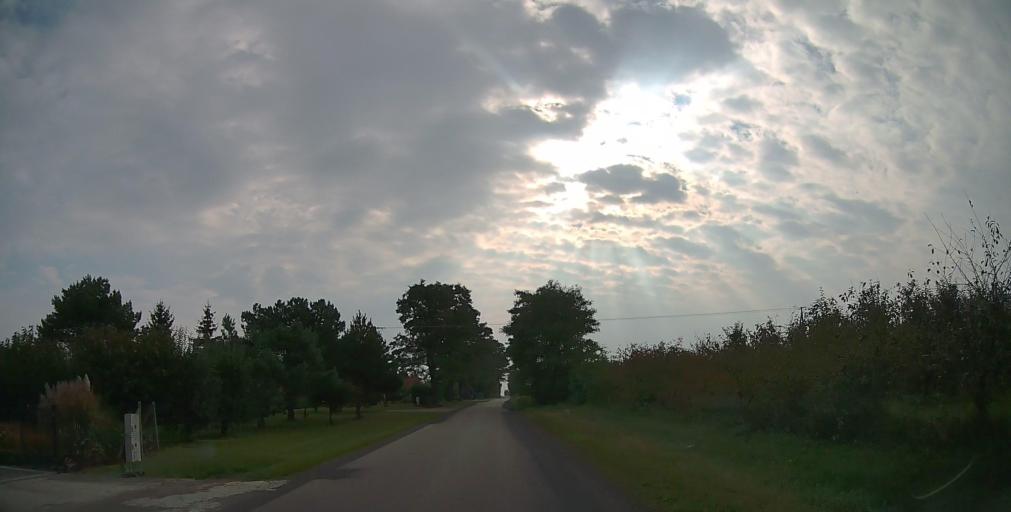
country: PL
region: Masovian Voivodeship
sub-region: Powiat grojecki
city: Mogielnica
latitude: 51.6571
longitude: 20.7168
